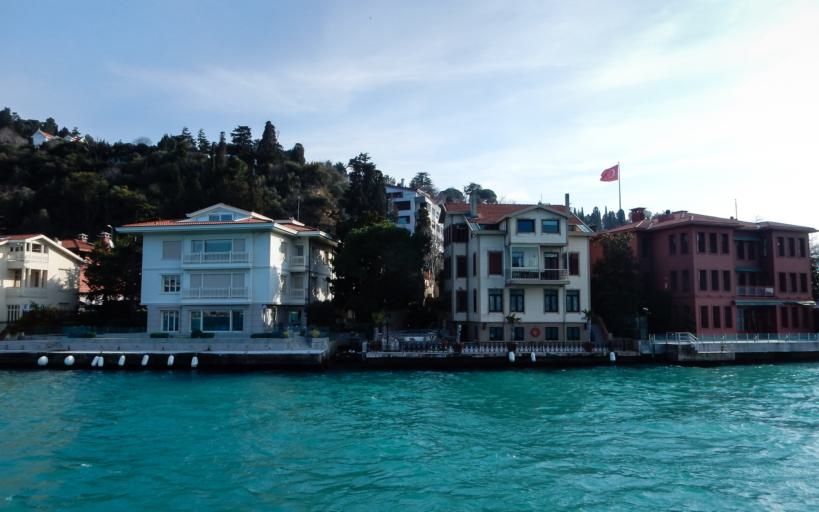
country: TR
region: Istanbul
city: UEskuedar
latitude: 41.0622
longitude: 29.0522
